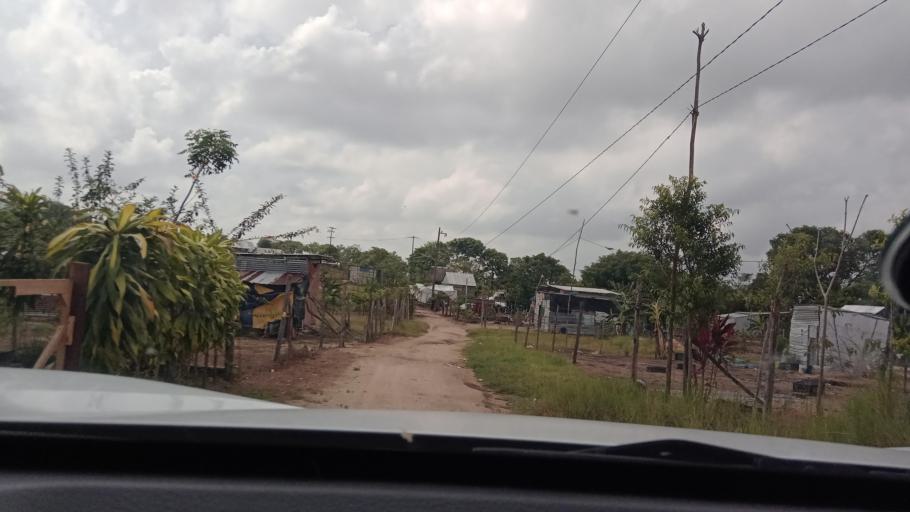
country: MX
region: Veracruz
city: Las Choapas
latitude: 17.8901
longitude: -94.1139
